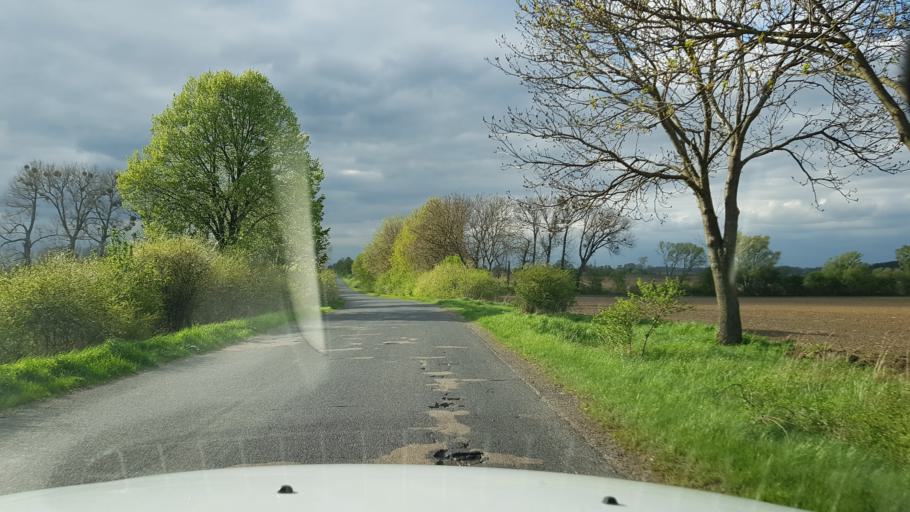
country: PL
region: West Pomeranian Voivodeship
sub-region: Powiat pyrzycki
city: Przelewice
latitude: 53.1355
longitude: 15.0380
